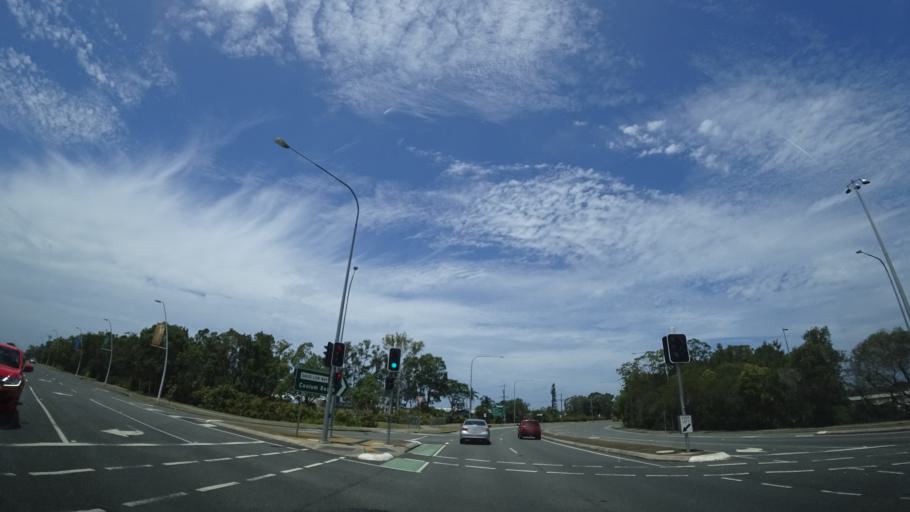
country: AU
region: Queensland
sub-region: Sunshine Coast
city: Mooloolaba
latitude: -26.6109
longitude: 153.0854
